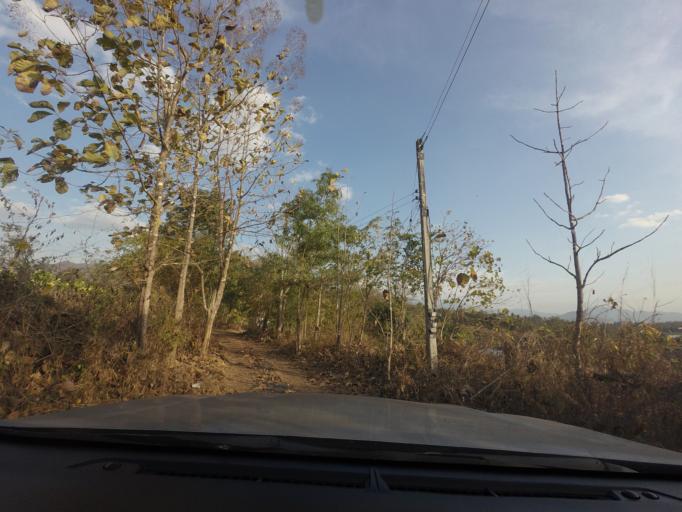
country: TH
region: Mae Hong Son
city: Mae Hi
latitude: 19.3401
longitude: 98.4280
